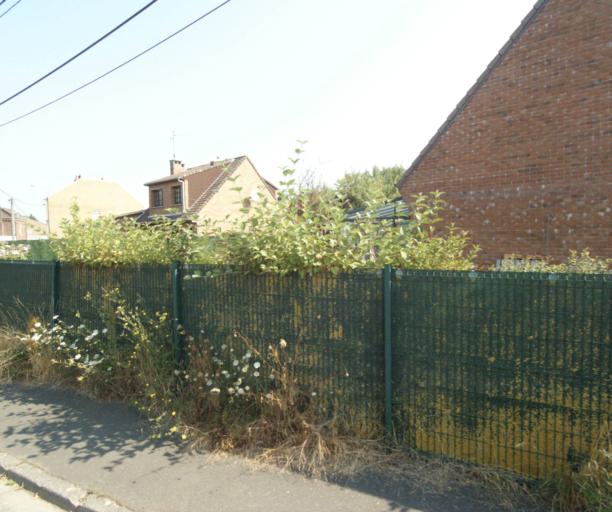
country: FR
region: Nord-Pas-de-Calais
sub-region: Departement du Nord
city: Quesnoy-sur-Deule
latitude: 50.7059
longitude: 2.9996
